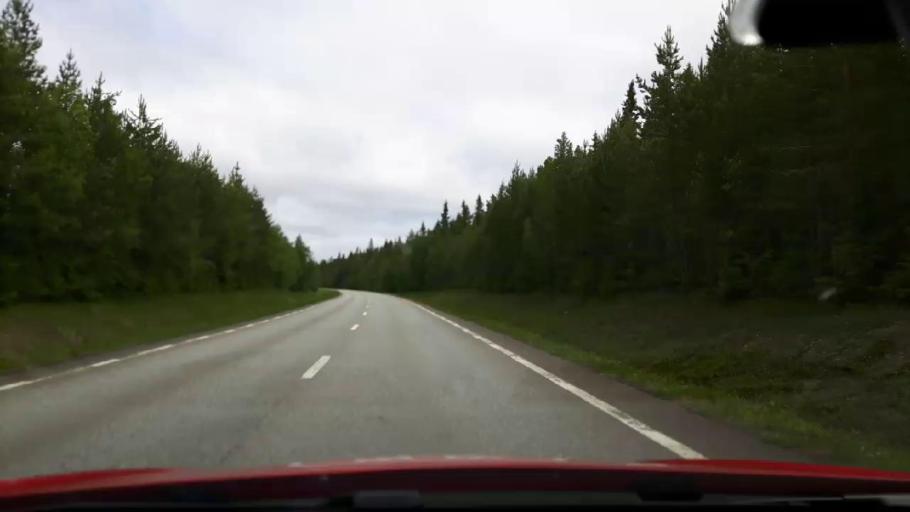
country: SE
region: Jaemtland
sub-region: Krokoms Kommun
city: Krokom
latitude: 63.4724
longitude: 14.5015
